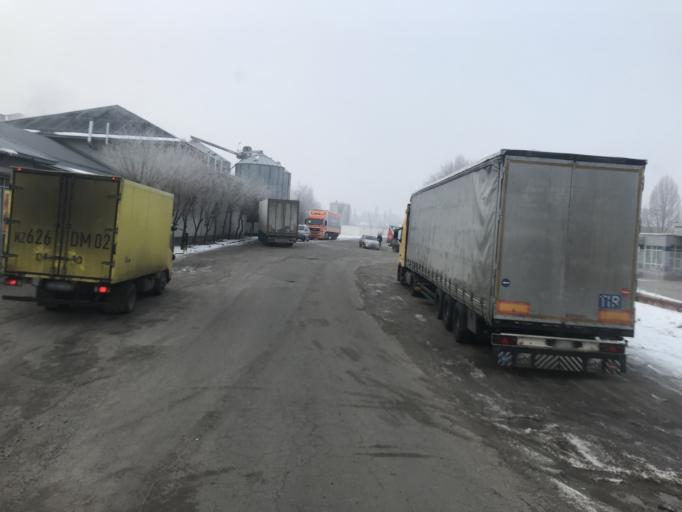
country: KZ
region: Almaty Oblysy
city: Pervomayskiy
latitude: 43.3612
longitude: 76.9777
